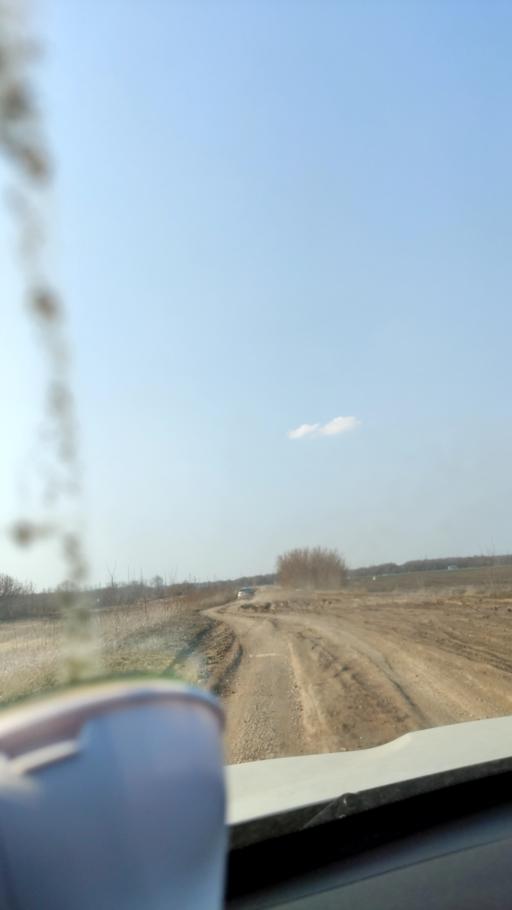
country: RU
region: Samara
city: Kinel'
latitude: 53.2575
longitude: 50.5283
